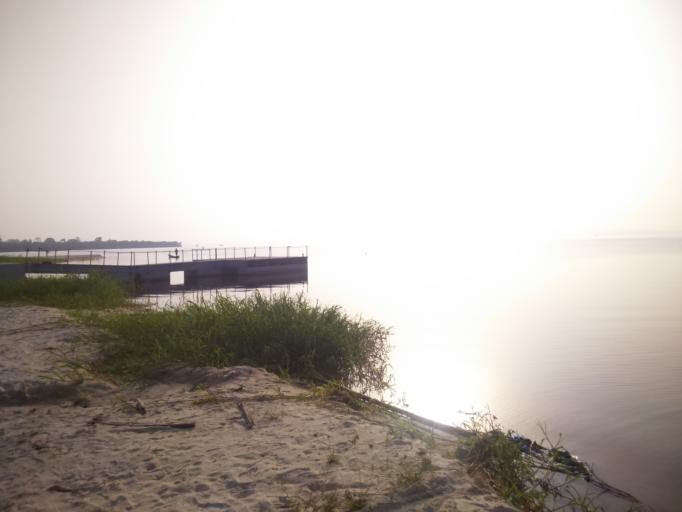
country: CI
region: Sud-Comoe
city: Adiake
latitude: 5.2865
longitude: -3.2904
